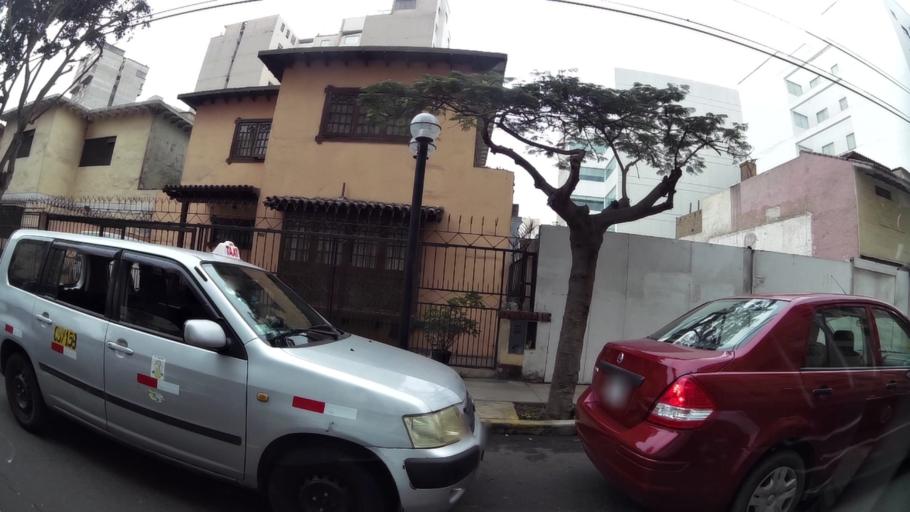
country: PE
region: Lima
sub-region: Lima
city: Surco
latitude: -12.1264
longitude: -77.0270
